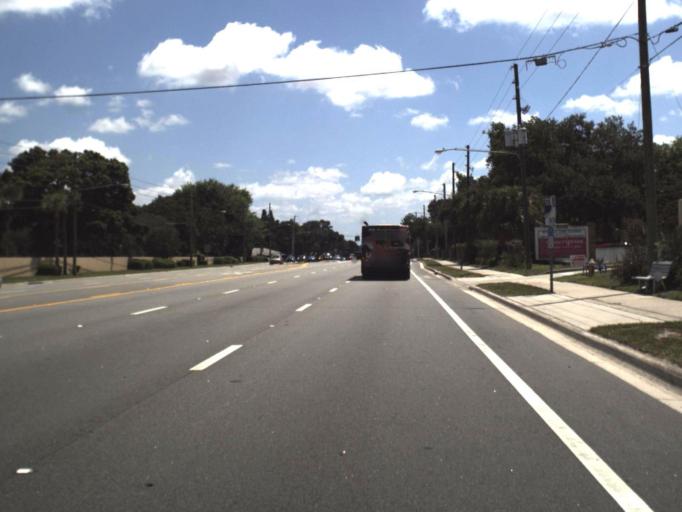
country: US
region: Florida
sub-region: Pinellas County
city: Saint George
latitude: 28.0194
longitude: -82.7277
